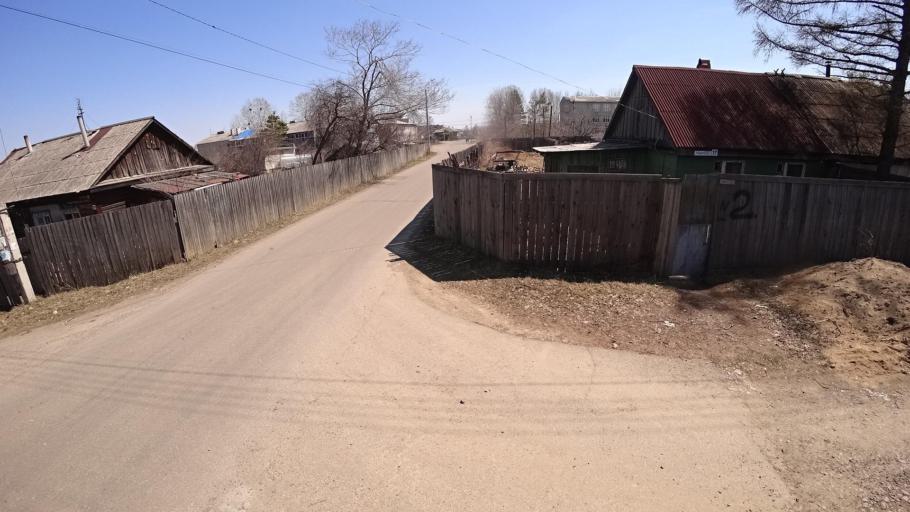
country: RU
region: Khabarovsk Krai
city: Khurba
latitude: 50.4051
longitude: 136.8854
